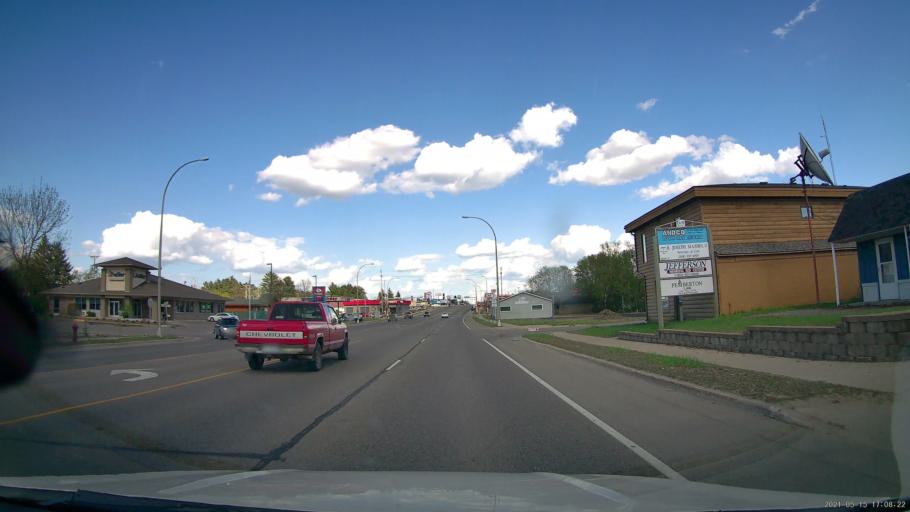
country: US
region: Minnesota
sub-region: Hubbard County
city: Park Rapids
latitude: 46.9221
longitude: -95.0499
